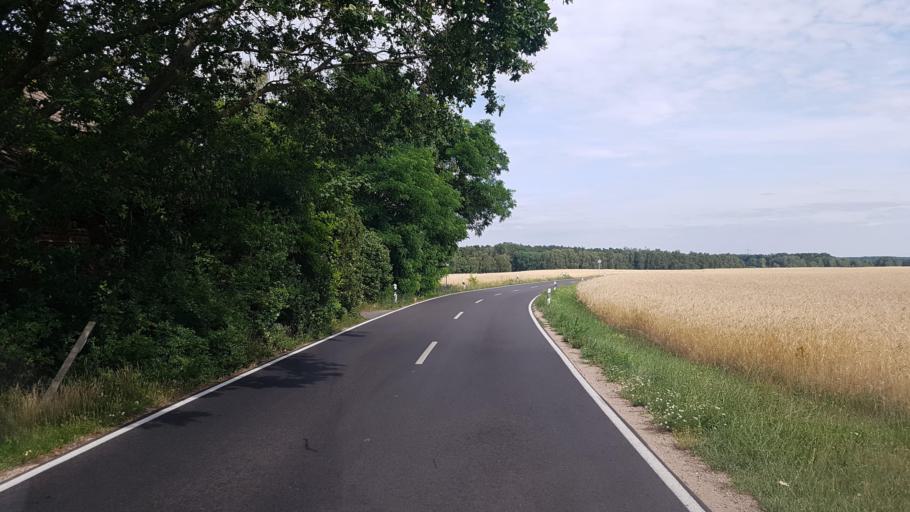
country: DE
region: Saxony-Anhalt
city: Abtsdorf
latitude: 51.9098
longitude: 12.6962
